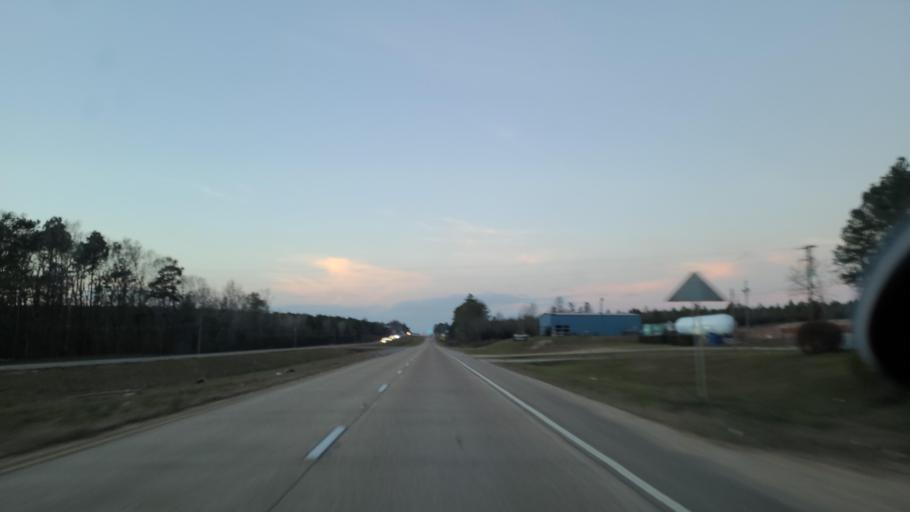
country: US
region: Mississippi
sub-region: Forrest County
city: Hattiesburg
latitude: 31.1773
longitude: -89.2473
